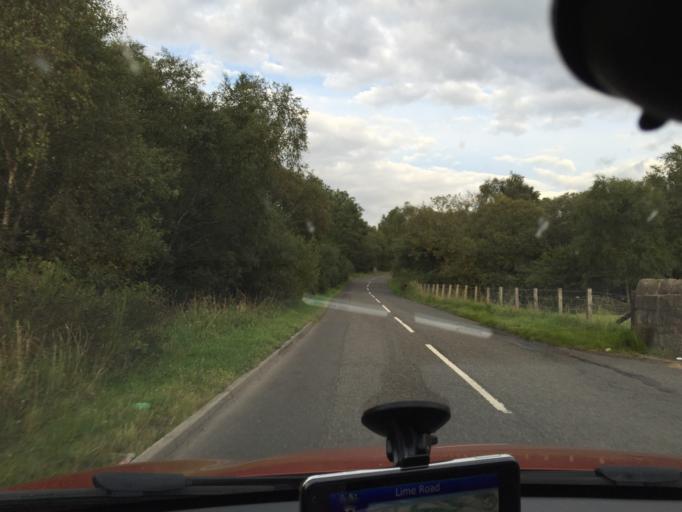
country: GB
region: Scotland
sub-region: Falkirk
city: Bonnybridge
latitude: 55.9929
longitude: -3.8548
